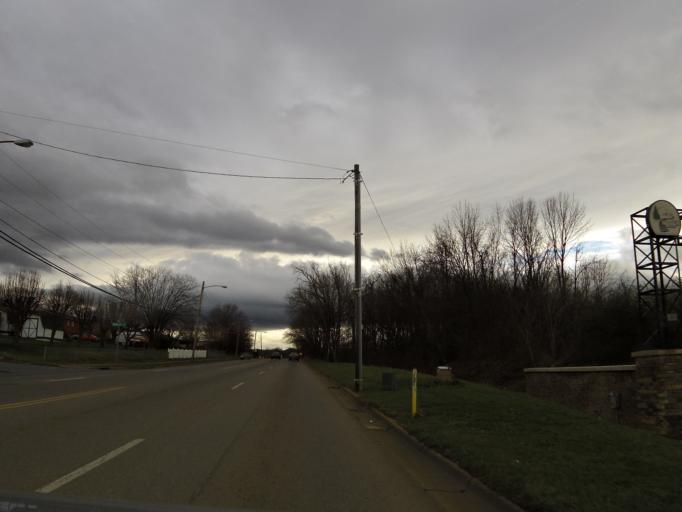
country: US
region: Tennessee
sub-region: Washington County
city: Johnson City
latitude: 36.3152
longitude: -82.3365
